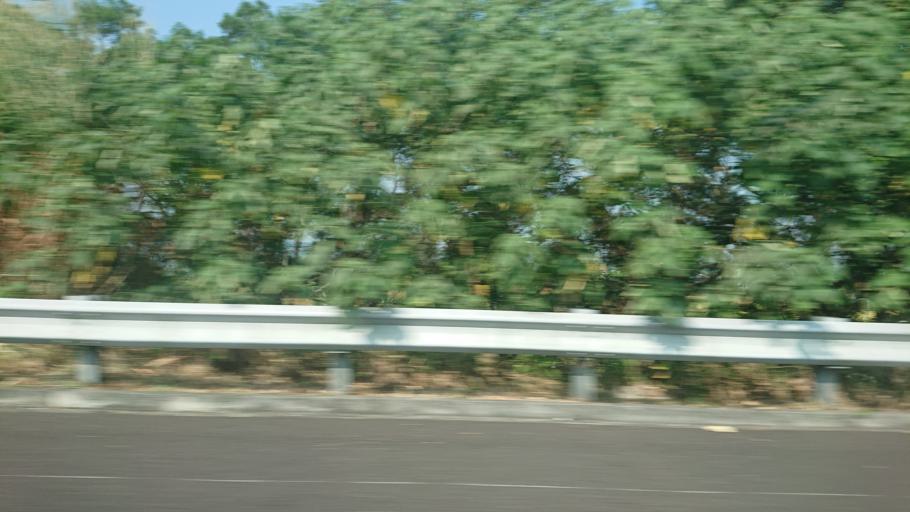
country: TW
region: Taiwan
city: Lugu
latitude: 23.8209
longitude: 120.7055
